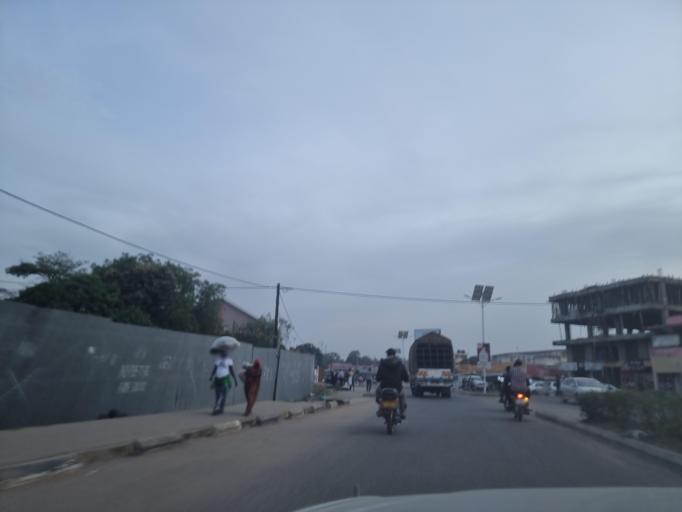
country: UG
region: Northern Region
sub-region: Arua District
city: Arua
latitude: 3.0226
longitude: 30.9127
